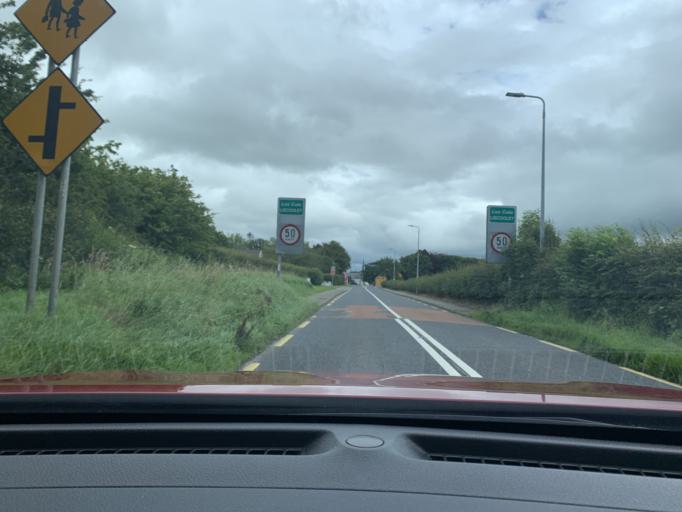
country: IE
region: Ulster
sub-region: County Donegal
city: Convoy
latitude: 54.8010
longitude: -7.6450
